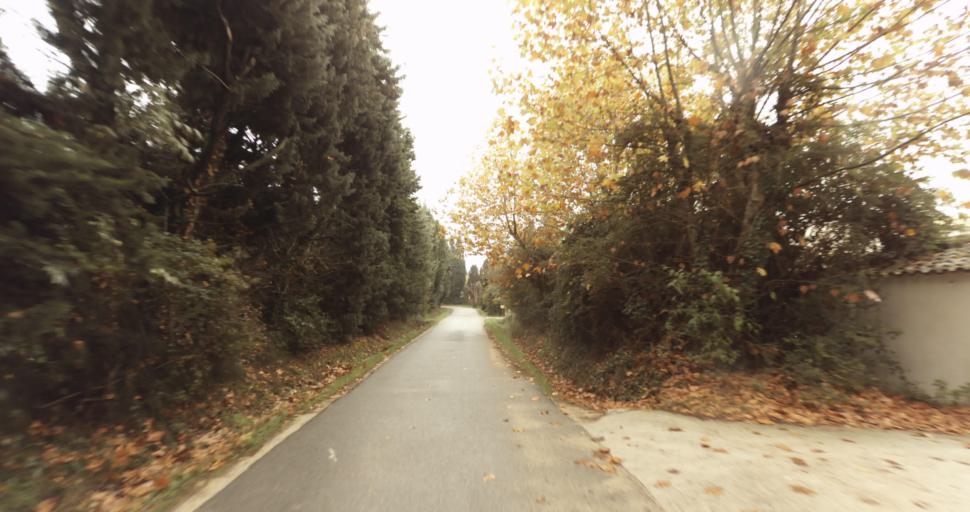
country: FR
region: Provence-Alpes-Cote d'Azur
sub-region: Departement des Bouches-du-Rhone
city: Rognonas
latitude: 43.9064
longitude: 4.8115
